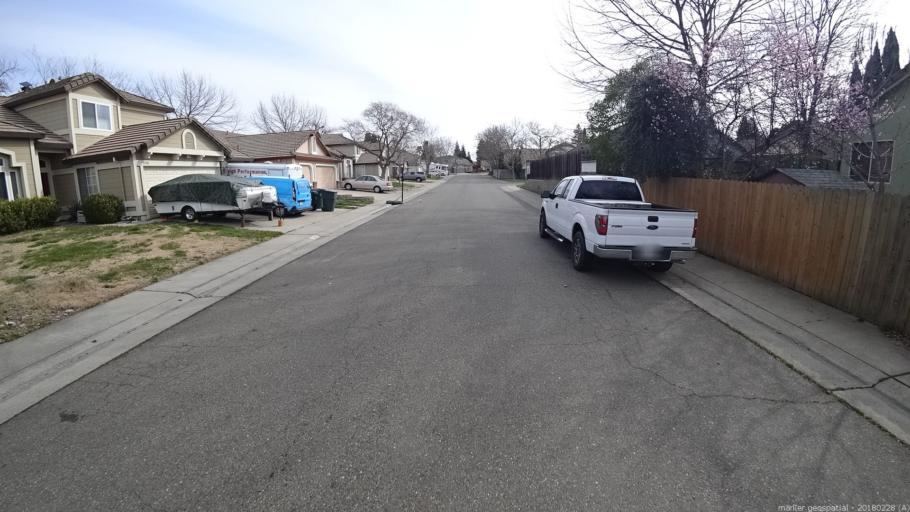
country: US
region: California
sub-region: Sacramento County
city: Antelope
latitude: 38.7245
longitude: -121.3396
